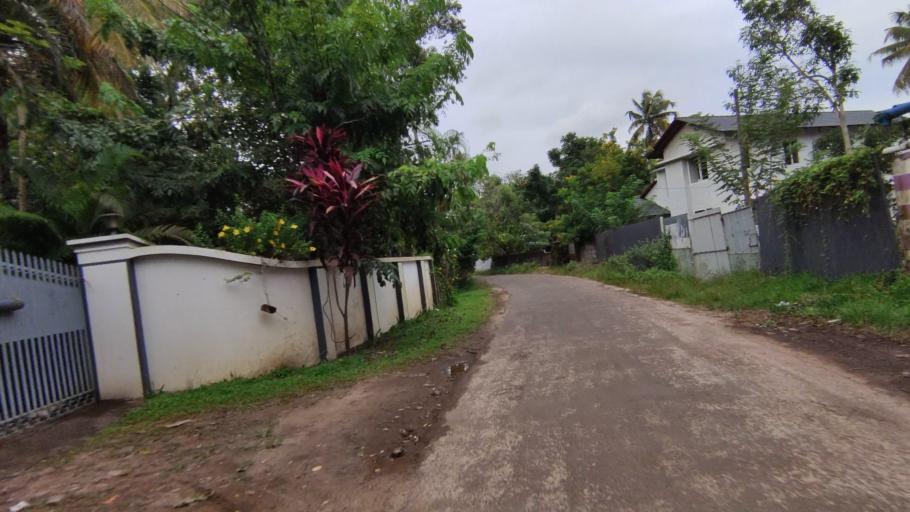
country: IN
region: Kerala
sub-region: Alappuzha
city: Shertallai
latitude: 9.6129
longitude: 76.3545
